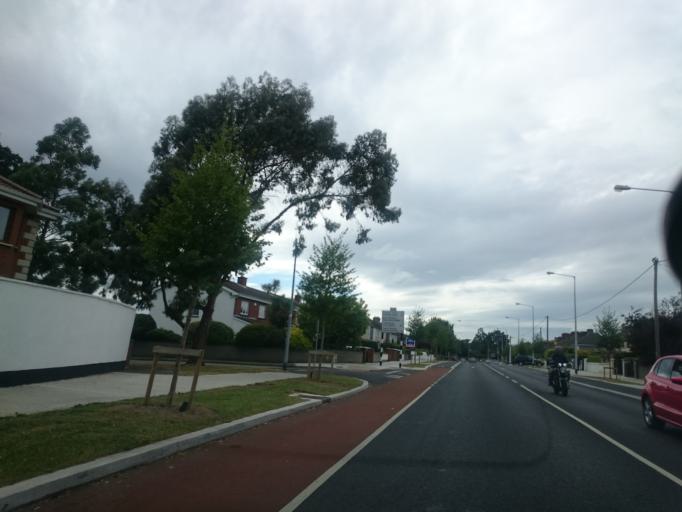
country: IE
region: Leinster
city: Dundrum
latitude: 53.3010
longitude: -6.2638
